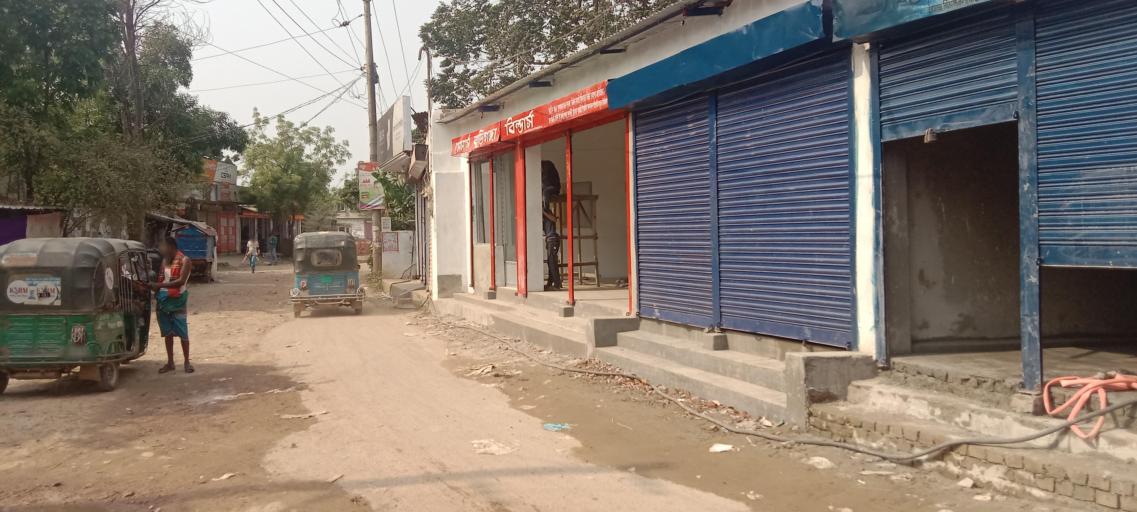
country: BD
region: Dhaka
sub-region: Dhaka
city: Dhaka
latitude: 23.6660
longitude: 90.4204
